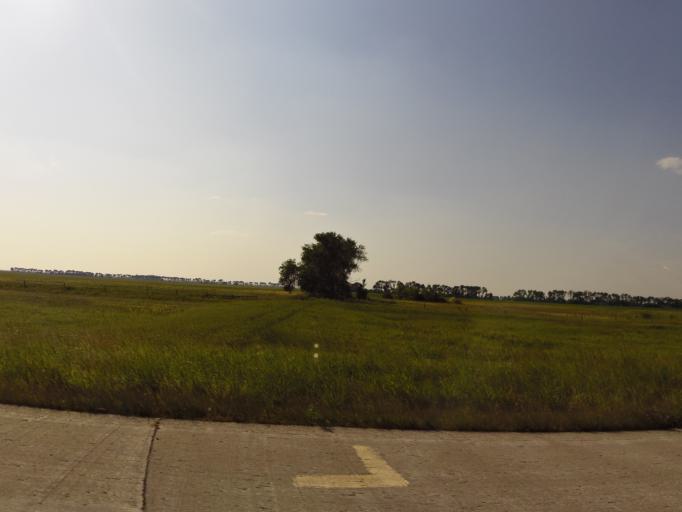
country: US
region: North Dakota
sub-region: Walsh County
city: Grafton
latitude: 48.3759
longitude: -97.1905
